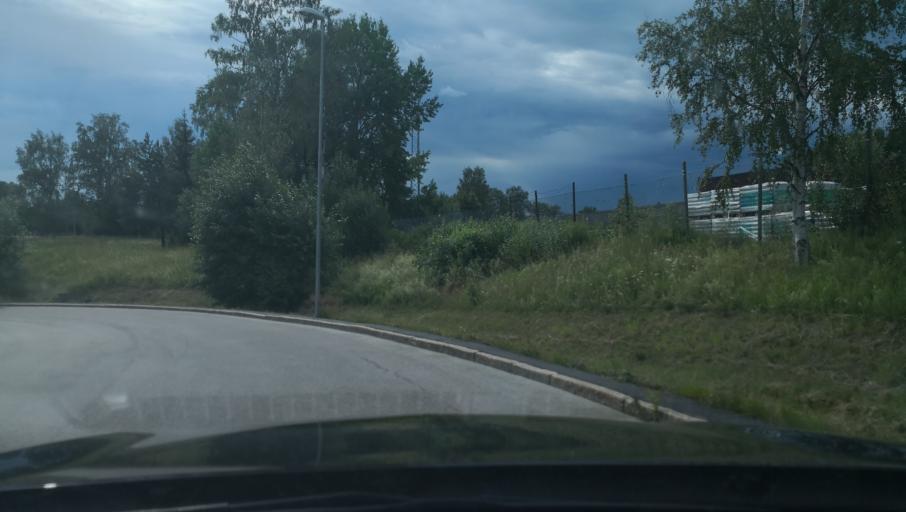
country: SE
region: Vaestmanland
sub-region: Fagersta Kommun
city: Fagersta
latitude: 59.9917
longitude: 15.8252
